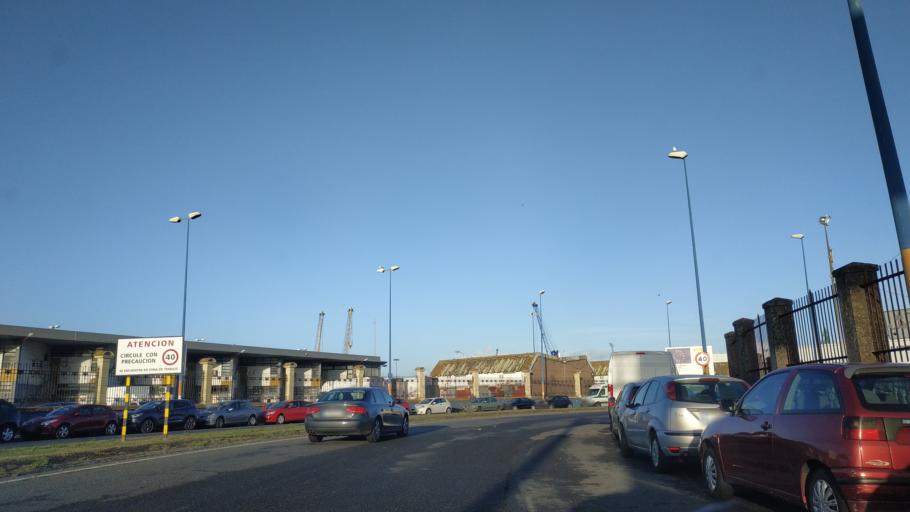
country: ES
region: Galicia
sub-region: Provincia da Coruna
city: A Coruna
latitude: 43.3584
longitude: -8.3988
